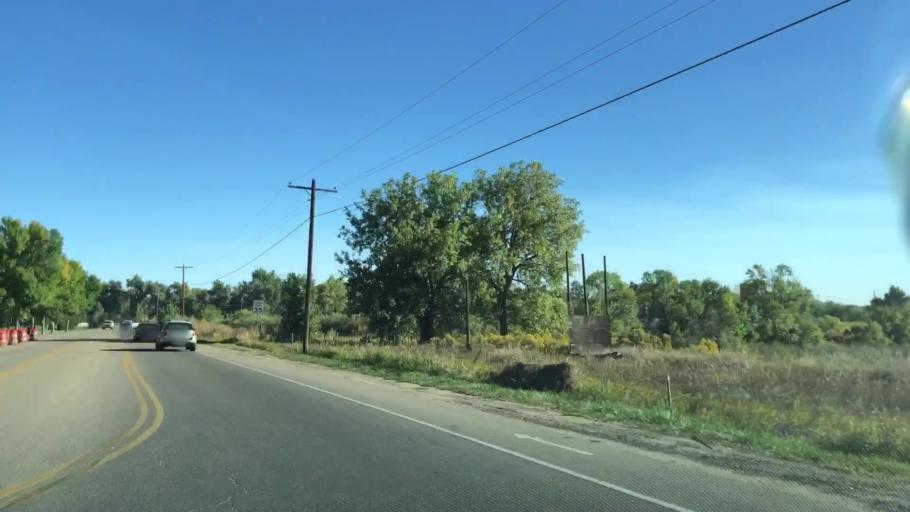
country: US
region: Colorado
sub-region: Larimer County
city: Loveland
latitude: 40.3962
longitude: -105.1250
